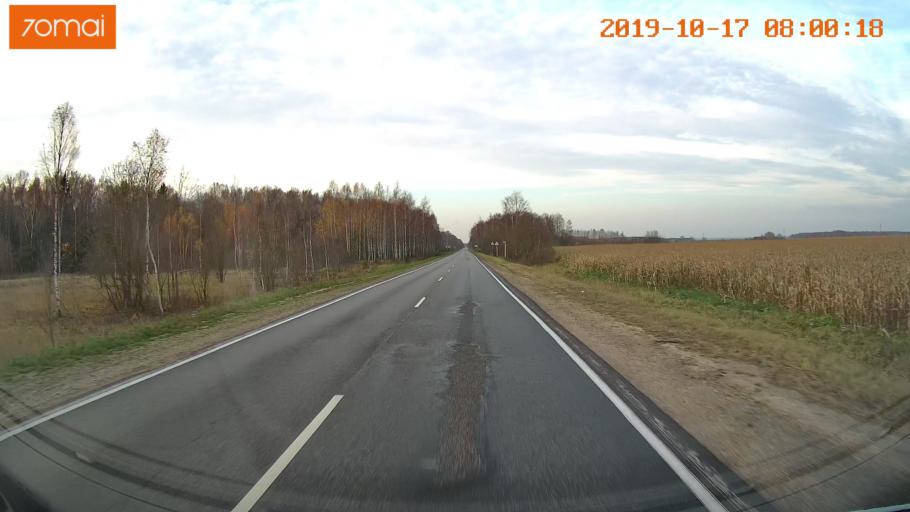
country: RU
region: Vladimir
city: Bavleny
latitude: 56.3848
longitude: 39.5209
